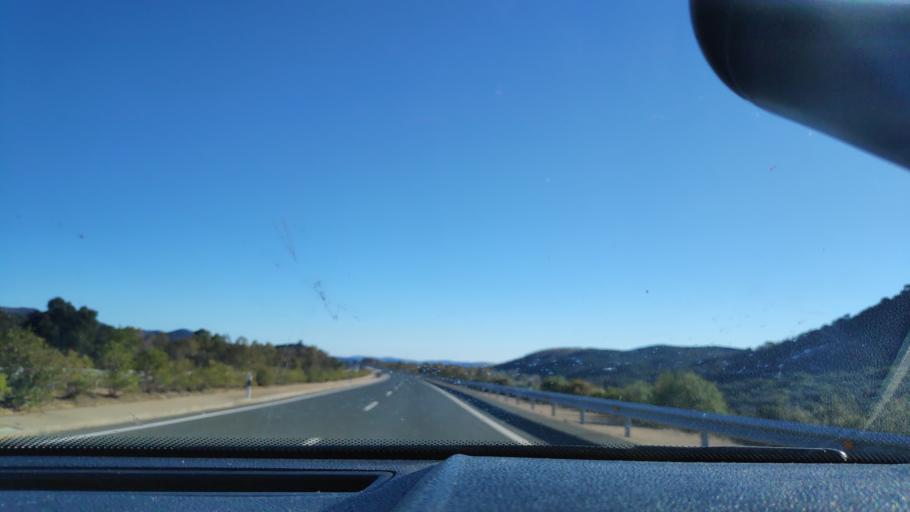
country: ES
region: Extremadura
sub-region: Provincia de Badajoz
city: Monesterio
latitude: 38.0506
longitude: -6.2365
